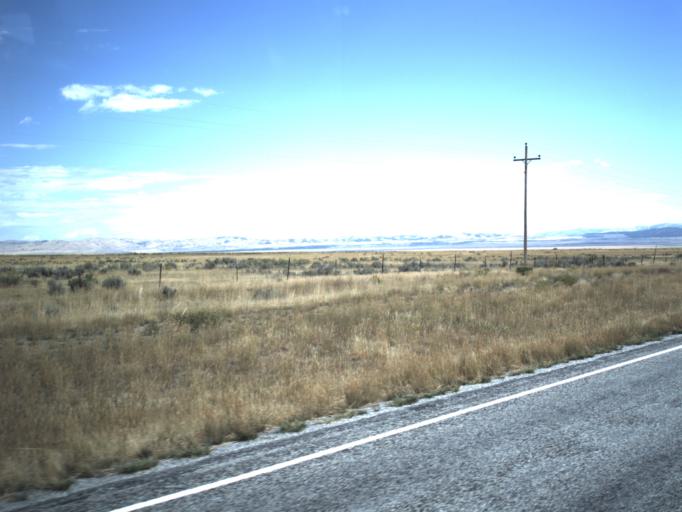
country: US
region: Idaho
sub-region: Oneida County
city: Malad City
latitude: 41.9655
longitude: -113.0293
